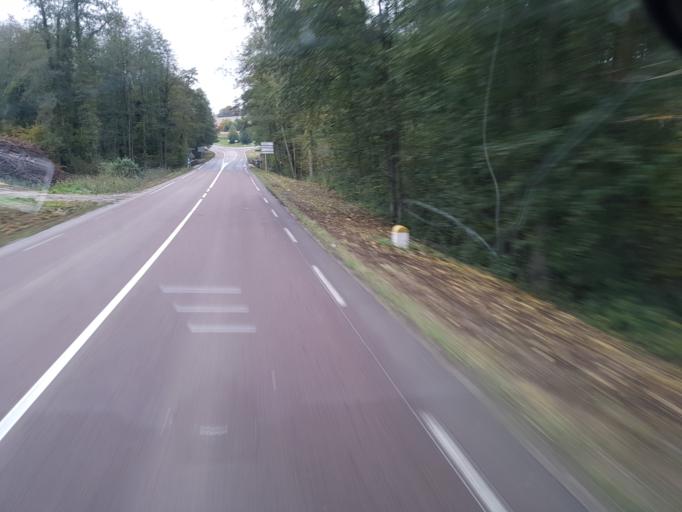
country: FR
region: Champagne-Ardenne
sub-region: Departement de la Marne
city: Montmirail
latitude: 48.8561
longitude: 3.5525
